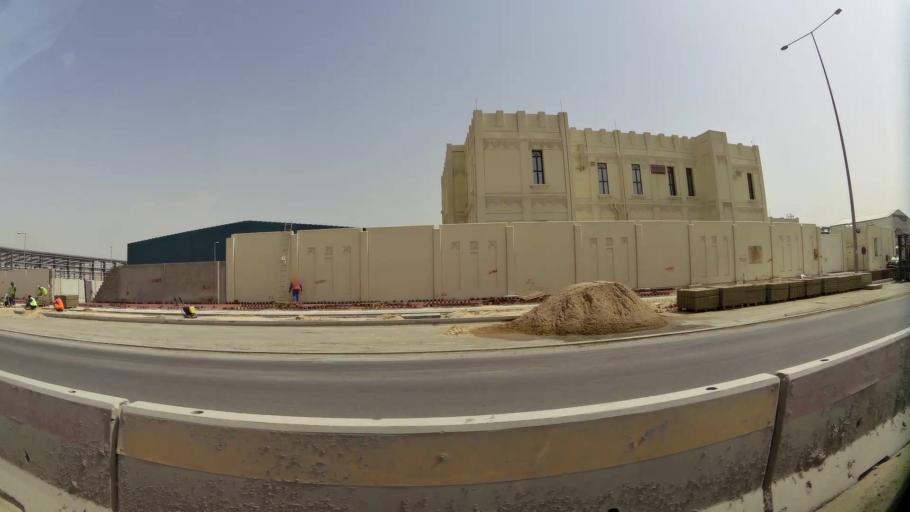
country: QA
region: Baladiyat ar Rayyan
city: Ar Rayyan
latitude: 25.2008
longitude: 51.4132
